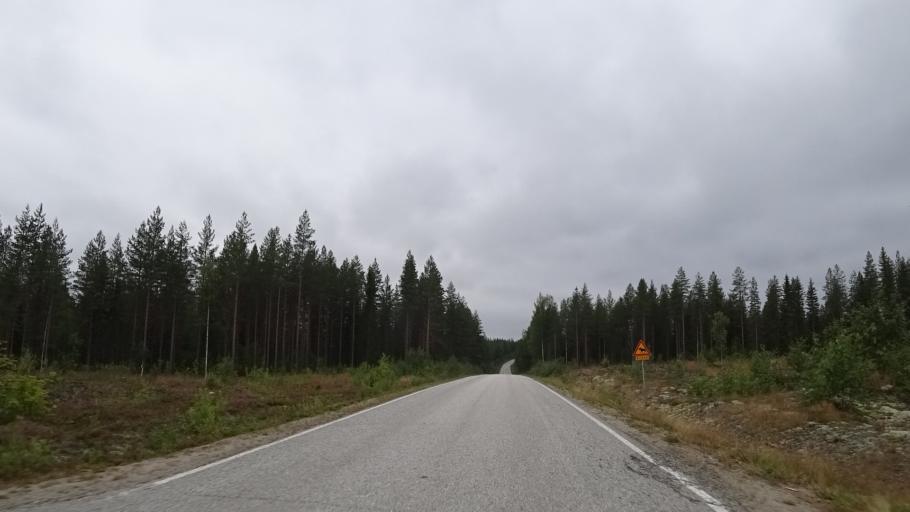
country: FI
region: North Karelia
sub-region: Pielisen Karjala
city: Lieksa
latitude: 63.3673
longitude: 30.2910
